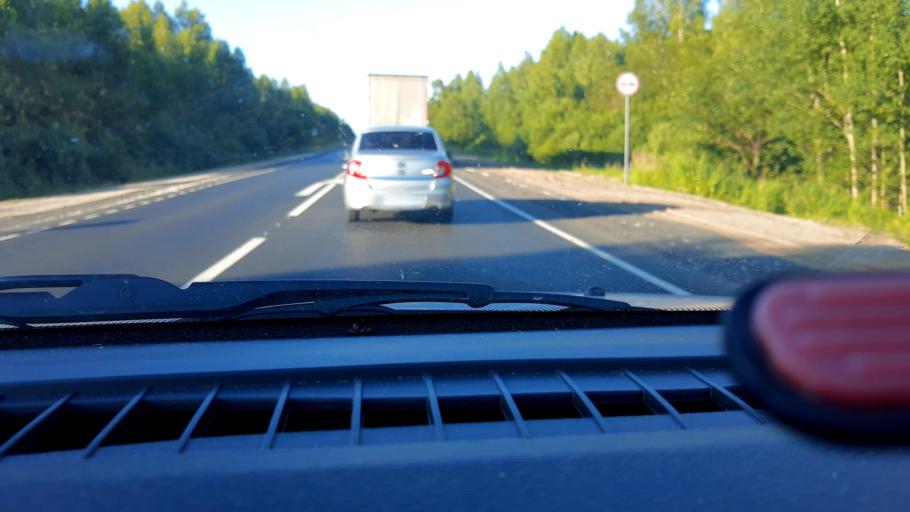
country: RU
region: Nizjnij Novgorod
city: Semenov
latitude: 56.7737
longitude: 44.4223
